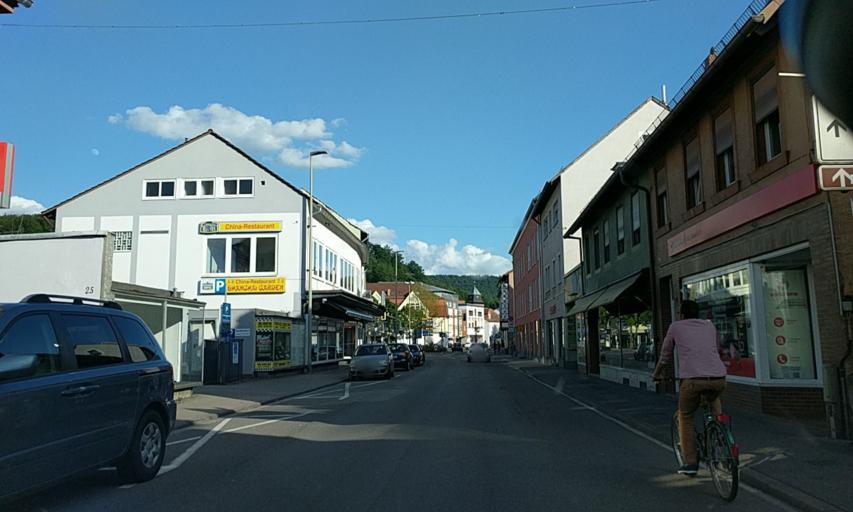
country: DE
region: Rheinland-Pfalz
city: Landstuhl
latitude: 49.4134
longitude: 7.5673
